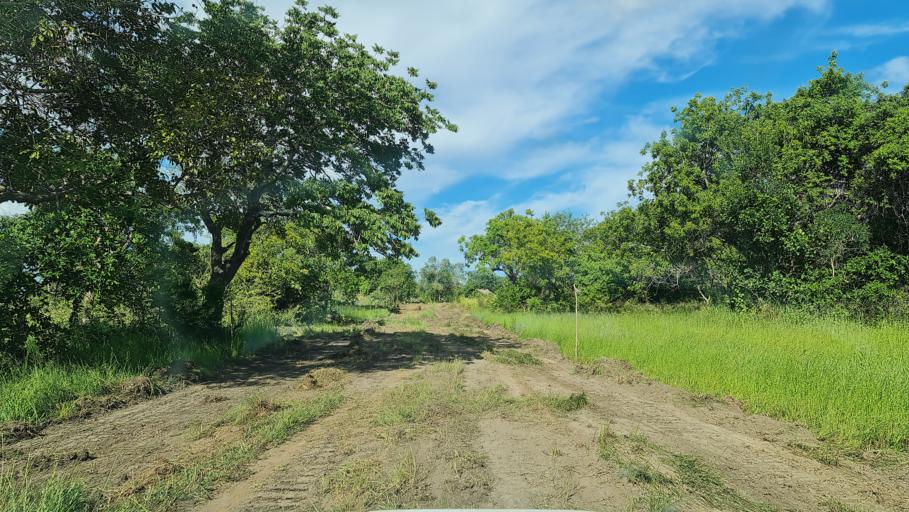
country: MZ
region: Nampula
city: Ilha de Mocambique
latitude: -15.5062
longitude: 40.1482
